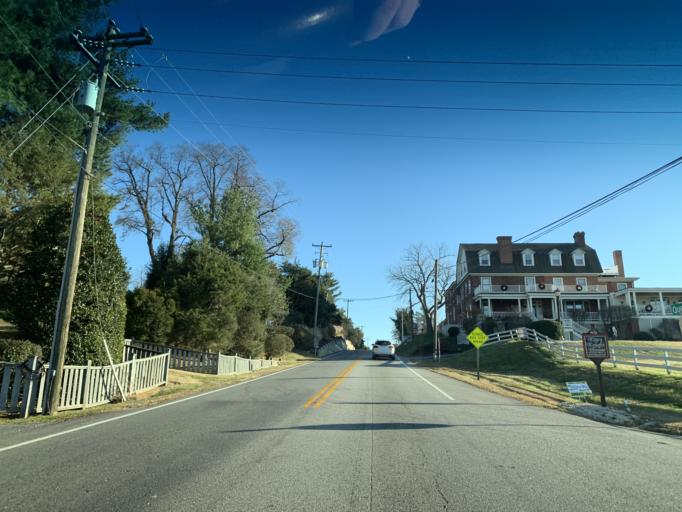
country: US
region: Delaware
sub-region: New Castle County
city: Middletown
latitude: 39.3616
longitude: -75.8804
